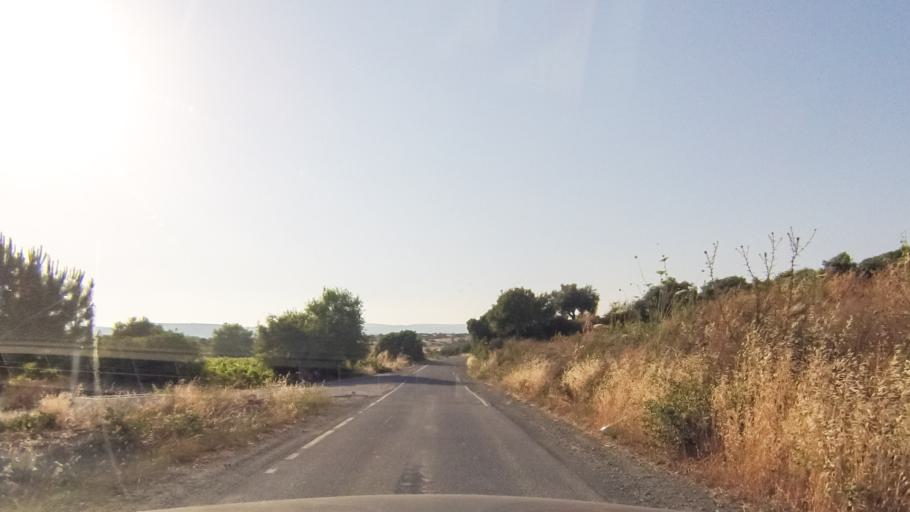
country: CY
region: Limassol
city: Pissouri
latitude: 34.6745
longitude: 32.7619
